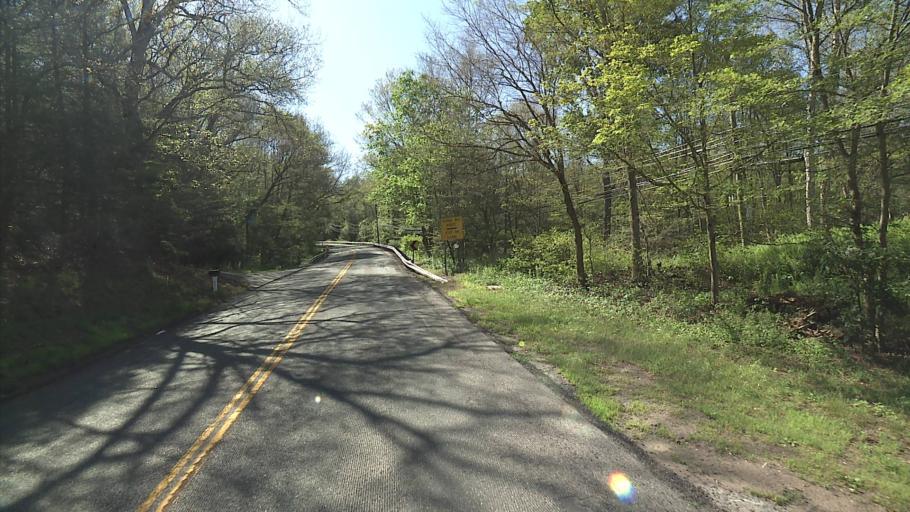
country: US
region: Connecticut
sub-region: Middlesex County
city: Moodus
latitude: 41.5502
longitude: -72.4459
